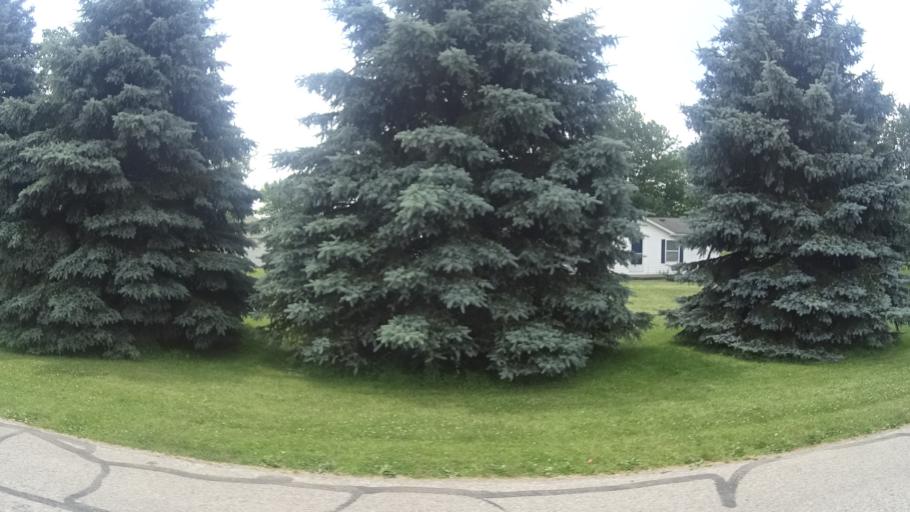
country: US
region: Ohio
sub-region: Huron County
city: Monroeville
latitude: 41.3109
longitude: -82.6987
